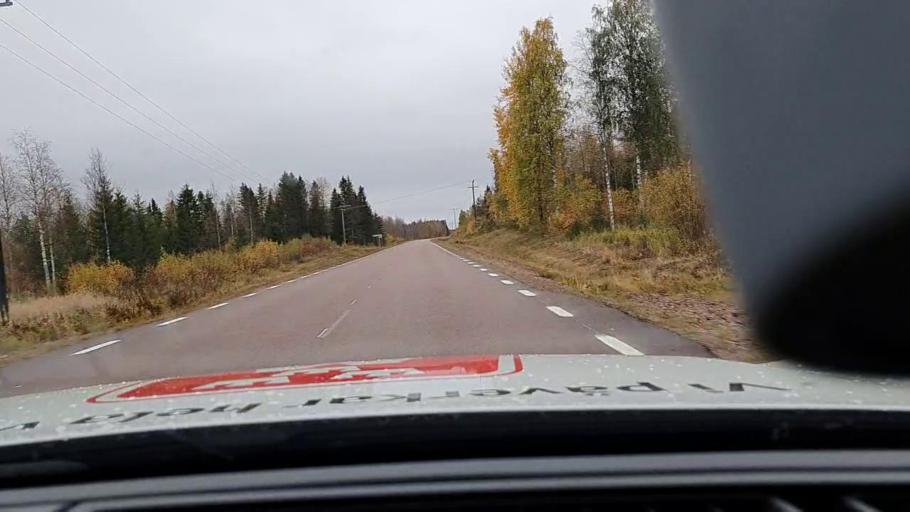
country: FI
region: Lapland
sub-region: Torniolaakso
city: Ylitornio
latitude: 66.1299
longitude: 23.9088
